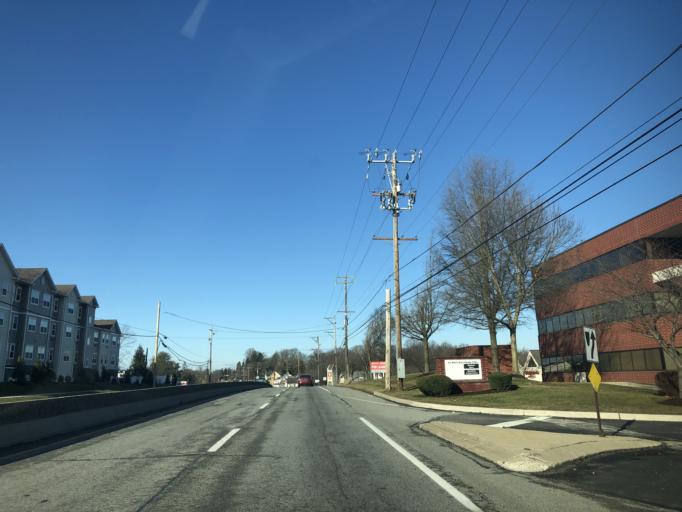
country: US
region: Pennsylvania
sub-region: Delaware County
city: Chester Heights
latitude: 39.8967
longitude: -75.4831
